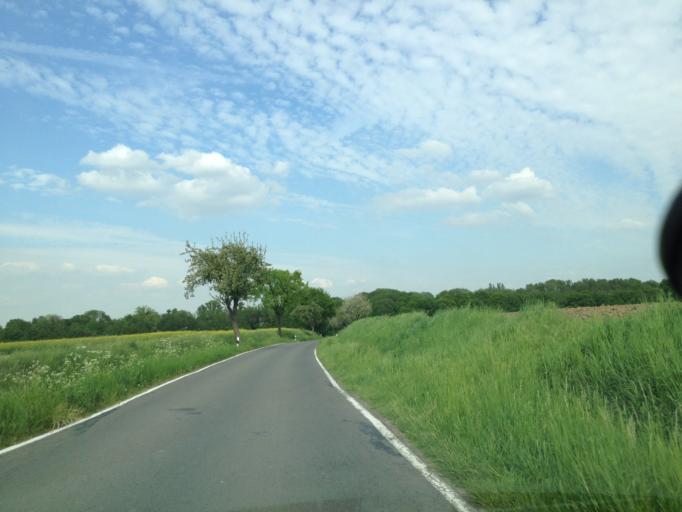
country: DE
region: North Rhine-Westphalia
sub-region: Regierungsbezirk Arnsberg
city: Welver
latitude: 51.5342
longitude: 8.0167
